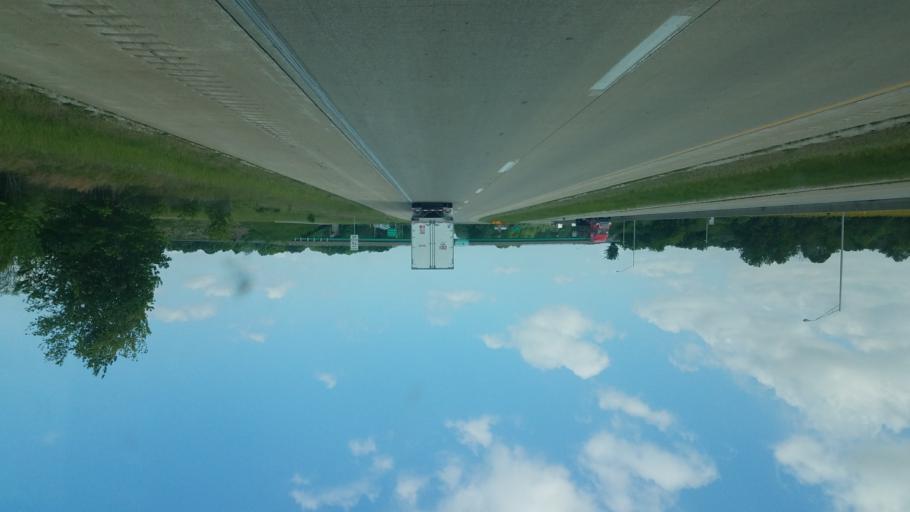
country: US
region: Indiana
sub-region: Vigo County
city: West Terre Haute
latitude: 39.4363
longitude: -87.5328
